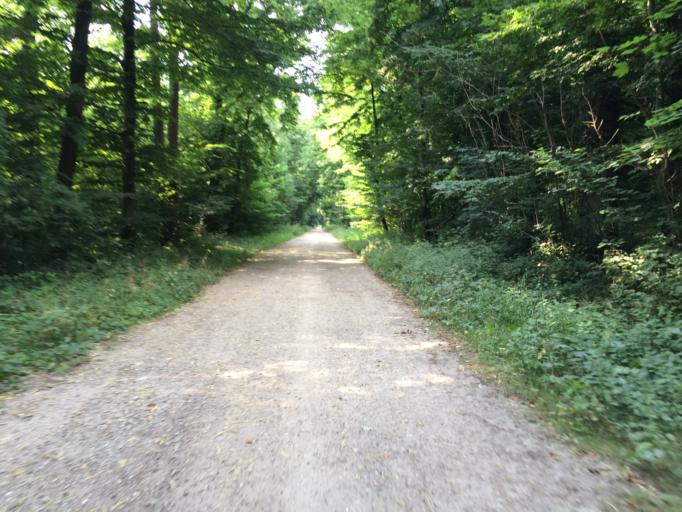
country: FR
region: Ile-de-France
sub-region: Departement de l'Essonne
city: Bievres
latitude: 48.7616
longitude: 2.2425
